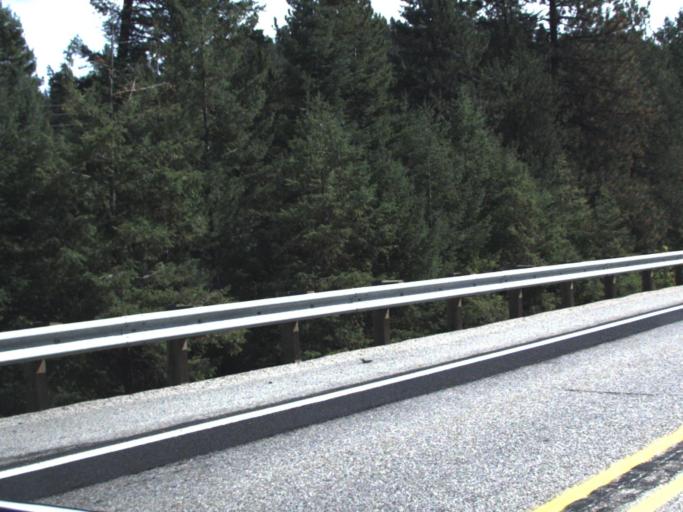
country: US
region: Washington
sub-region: Stevens County
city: Chewelah
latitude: 48.1405
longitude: -117.6587
